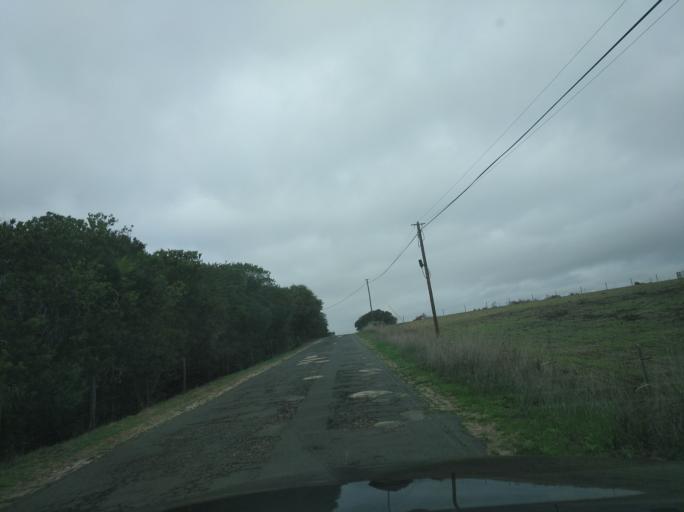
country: PT
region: Setubal
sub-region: Sines
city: Porto Covo
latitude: 37.8348
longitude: -8.7871
